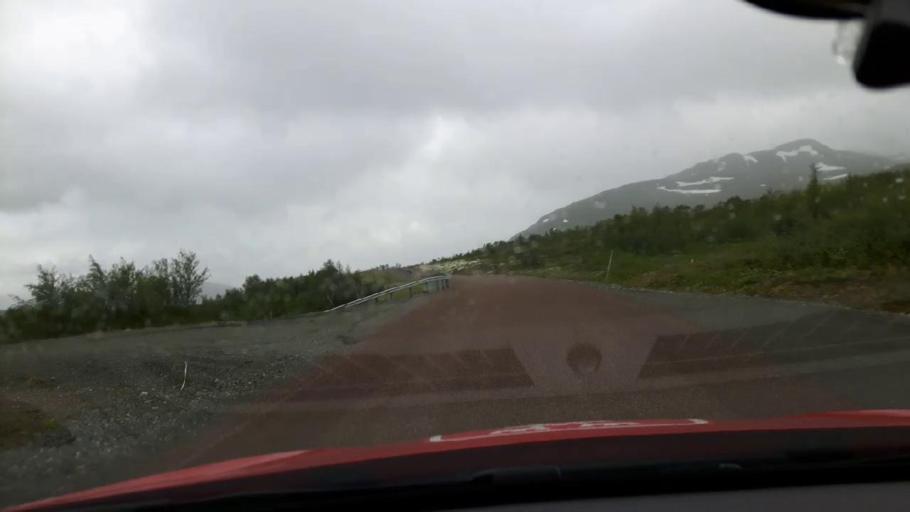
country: NO
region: Nord-Trondelag
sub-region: Meraker
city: Meraker
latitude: 63.2016
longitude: 12.3921
